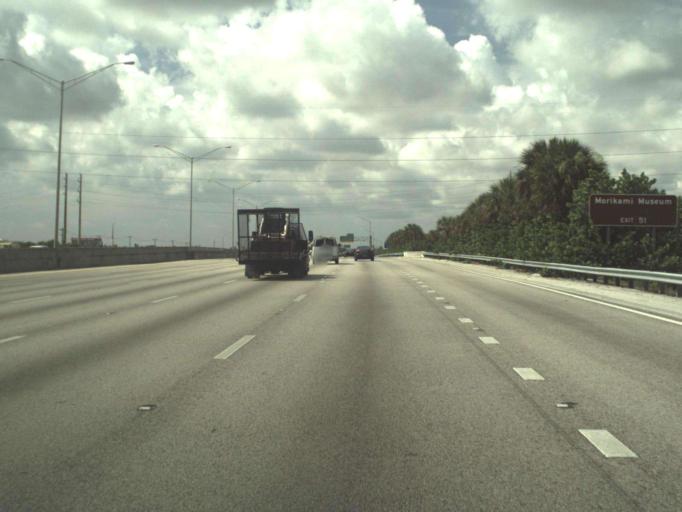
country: US
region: Florida
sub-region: Palm Beach County
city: Delray Beach
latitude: 26.4482
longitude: -80.0904
